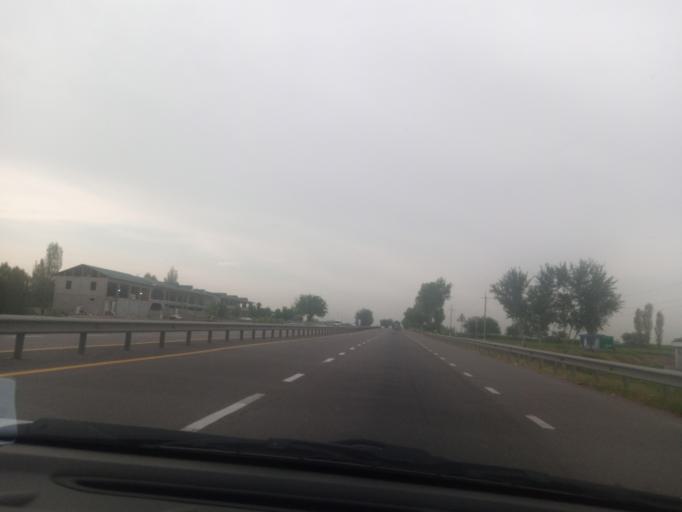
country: UZ
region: Toshkent Shahri
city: Bektemir
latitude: 41.1502
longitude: 69.4275
